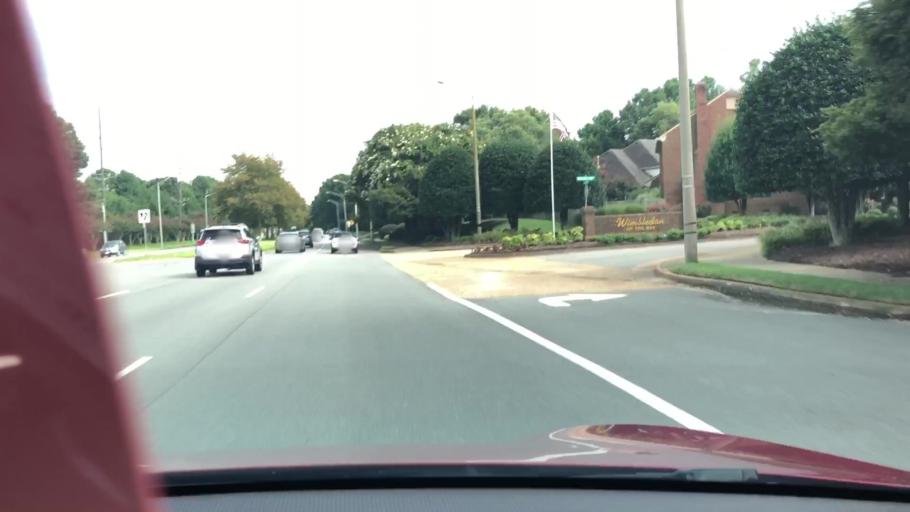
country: US
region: Virginia
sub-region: City of Virginia Beach
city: Virginia Beach
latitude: 36.8953
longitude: -76.0606
